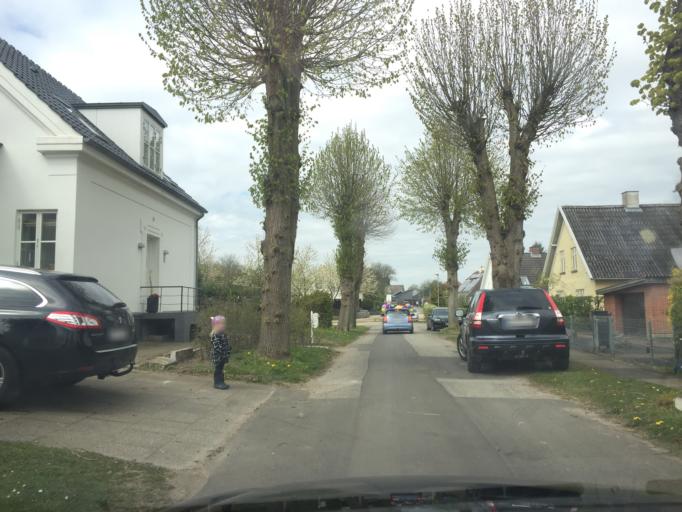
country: DK
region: South Denmark
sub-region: Kolding Kommune
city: Sonder Bjert
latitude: 55.4545
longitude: 9.5593
